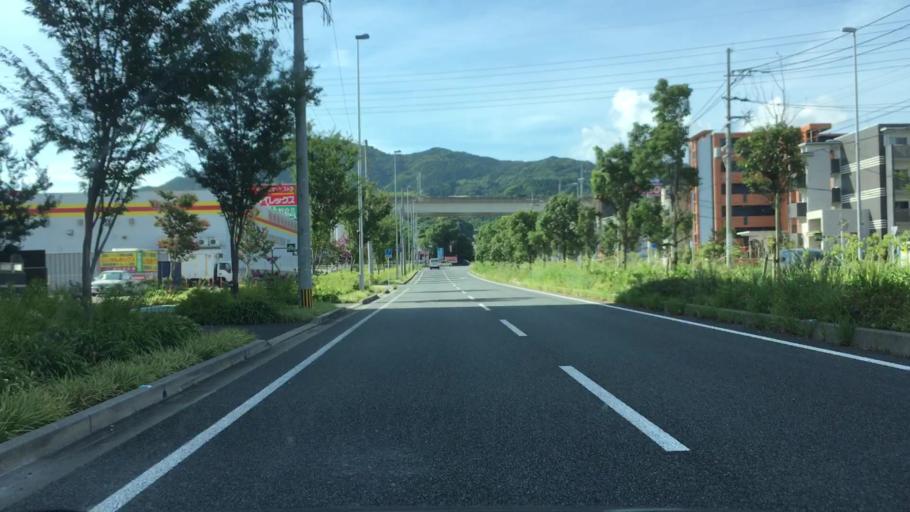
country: JP
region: Fukuoka
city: Maebaru-chuo
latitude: 33.5753
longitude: 130.2566
